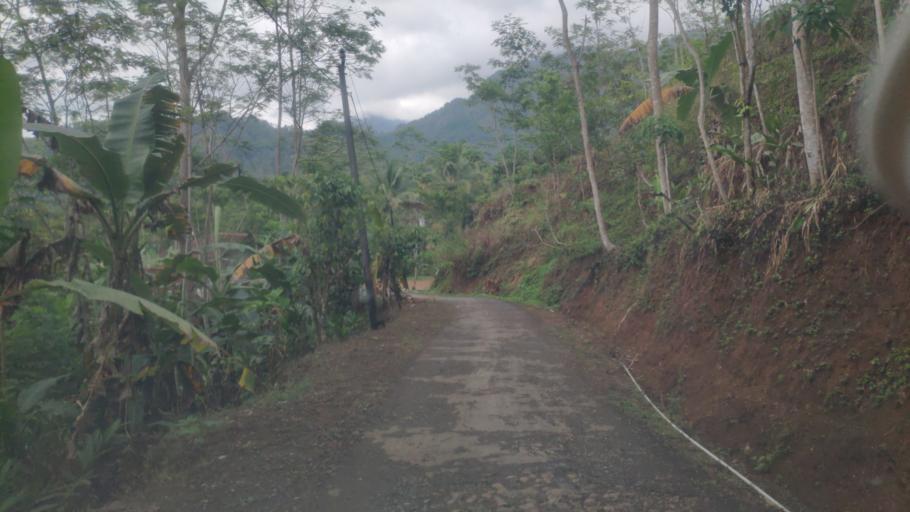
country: ID
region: Central Java
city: Purbalingga
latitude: -7.3032
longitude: 109.5721
